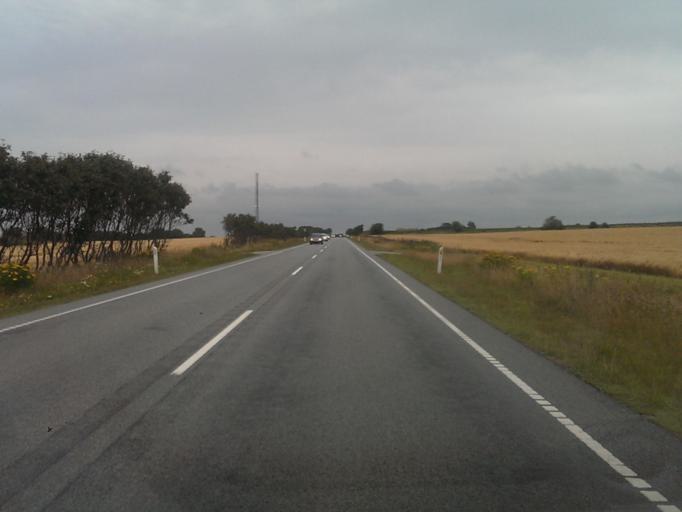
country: DK
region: South Denmark
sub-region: Esbjerg Kommune
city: Tjaereborg
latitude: 55.5465
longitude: 8.6272
